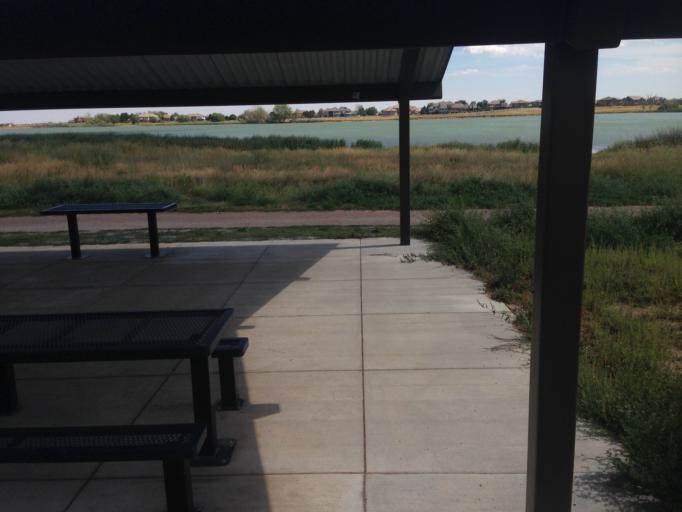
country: US
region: Colorado
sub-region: Adams County
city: Northglenn
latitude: 39.9536
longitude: -105.0169
